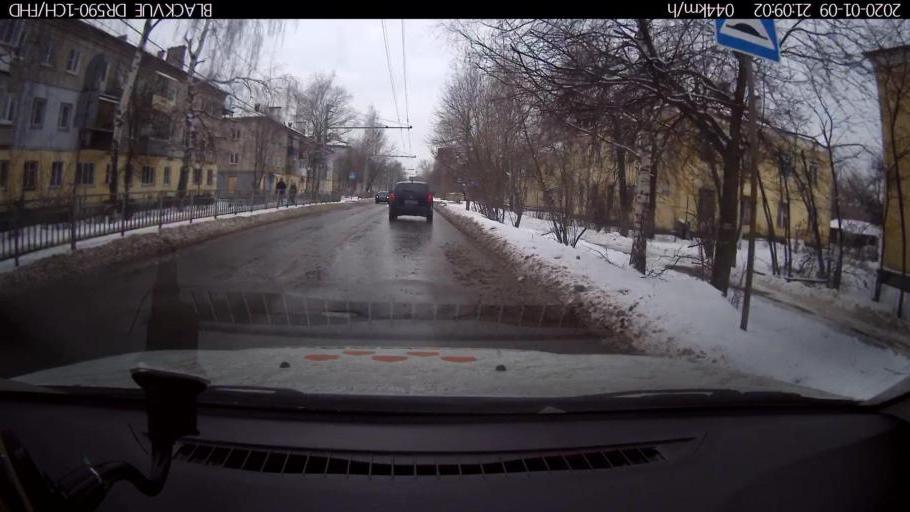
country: RU
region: Nizjnij Novgorod
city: Gorbatovka
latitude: 56.2919
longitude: 43.8597
